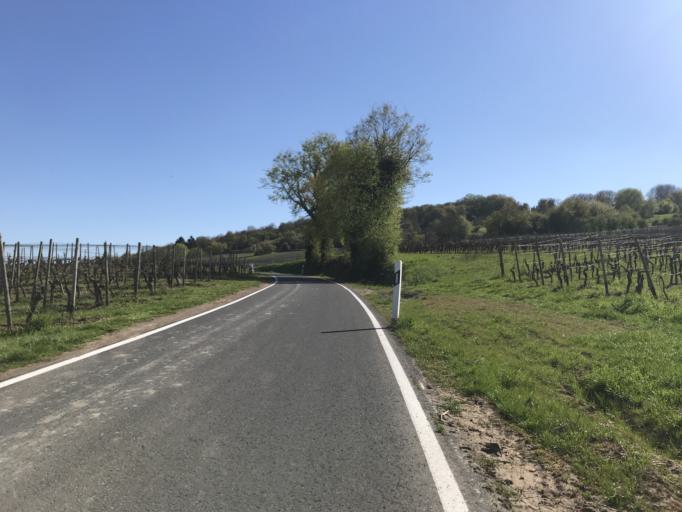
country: DE
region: Rheinland-Pfalz
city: Ingelheim am Rhein
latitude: 49.9538
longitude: 8.0539
